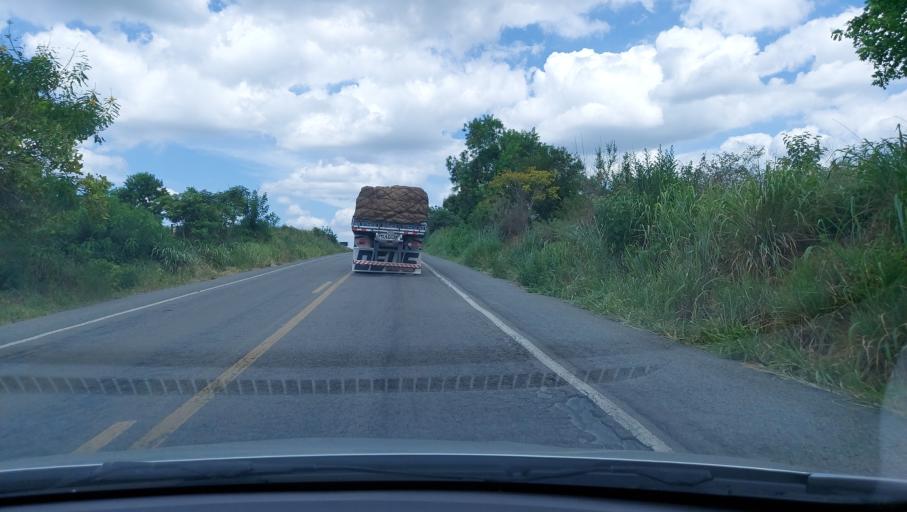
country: BR
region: Bahia
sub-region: Ruy Barbosa
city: Terra Nova
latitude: -12.4444
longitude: -40.7860
